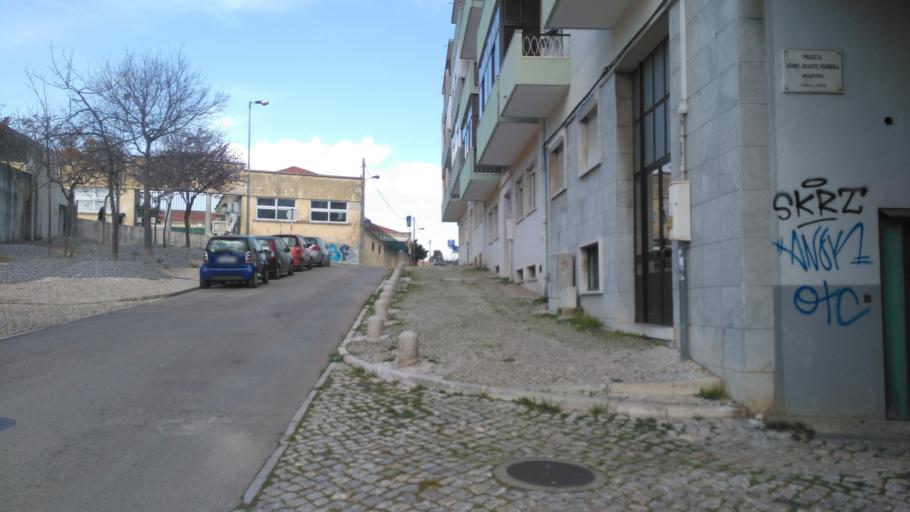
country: PT
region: Setubal
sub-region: Almada
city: Almada
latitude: 38.6812
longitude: -9.1606
